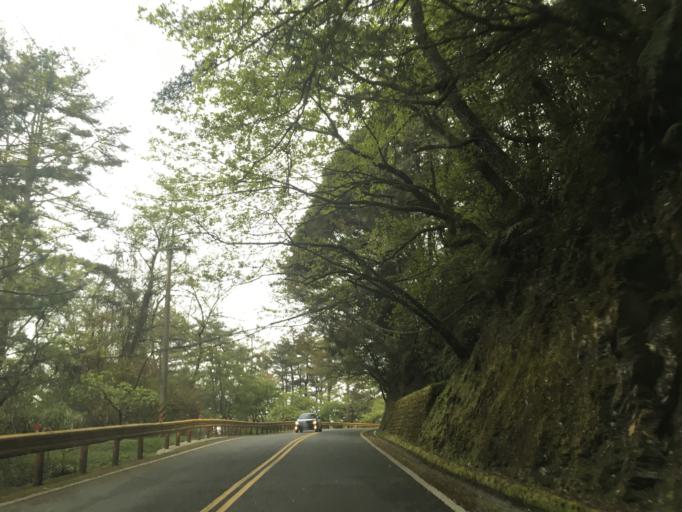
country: TW
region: Taiwan
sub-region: Hualien
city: Hualian
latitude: 24.1852
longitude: 121.3258
